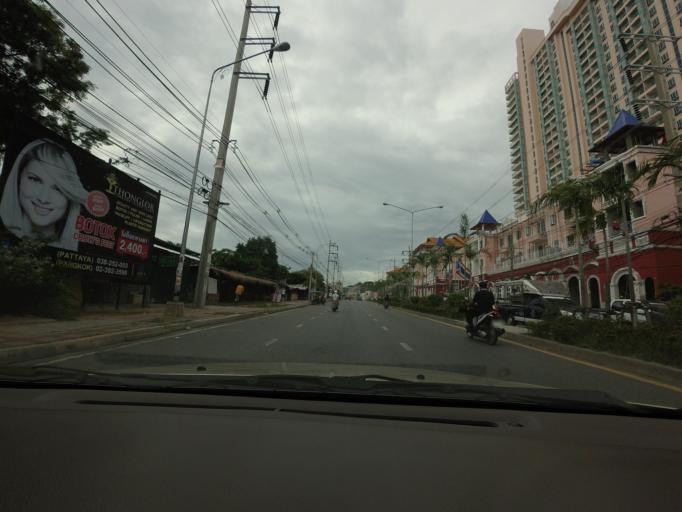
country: TH
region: Chon Buri
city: Phatthaya
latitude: 12.9071
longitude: 100.8689
